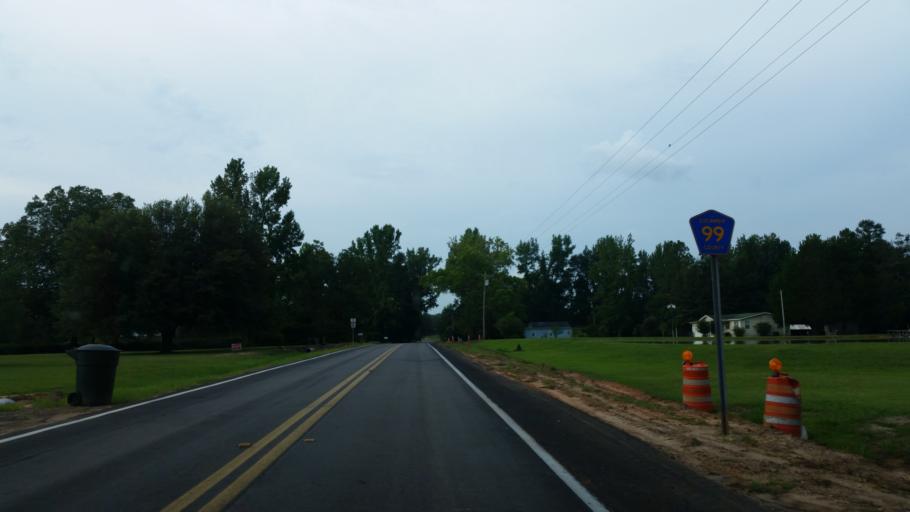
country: US
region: Florida
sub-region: Escambia County
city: Molino
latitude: 30.7731
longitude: -87.4789
